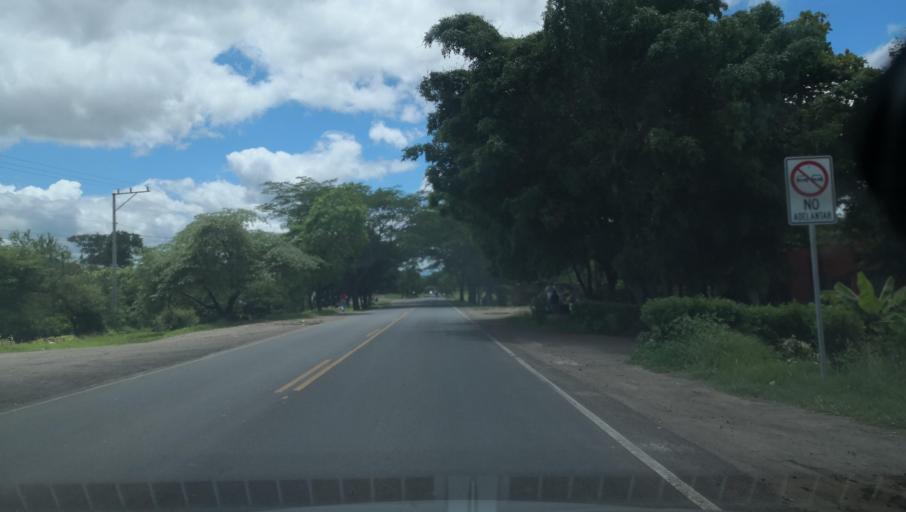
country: NI
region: Esteli
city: Esteli
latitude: 13.1622
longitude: -86.3688
